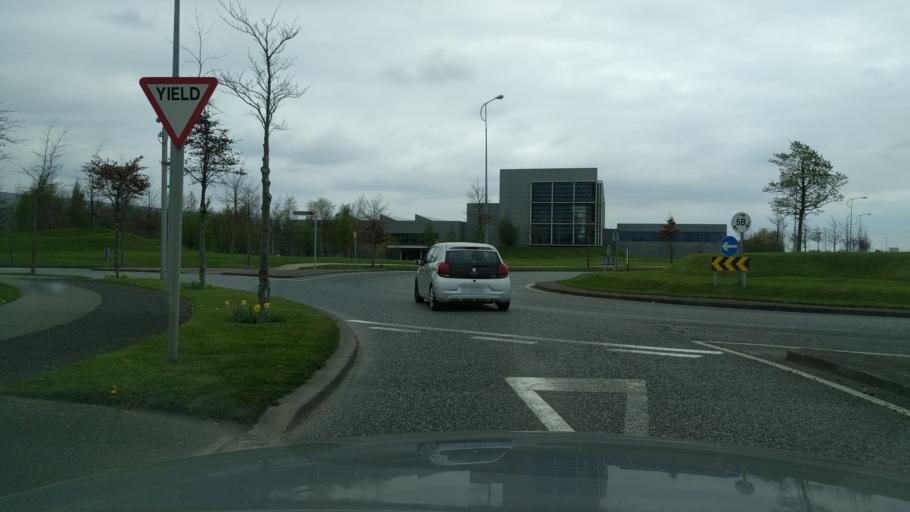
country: IE
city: Jobstown
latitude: 53.2911
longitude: -6.4144
